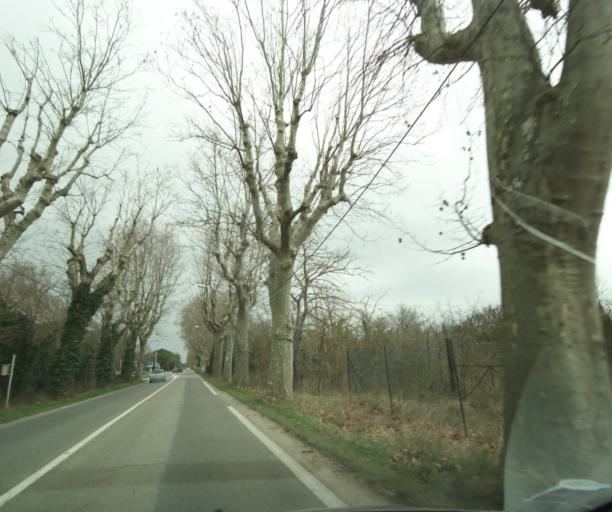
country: FR
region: Provence-Alpes-Cote d'Azur
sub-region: Departement des Bouches-du-Rhone
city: Aix-en-Provence
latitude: 43.5629
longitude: 5.4632
